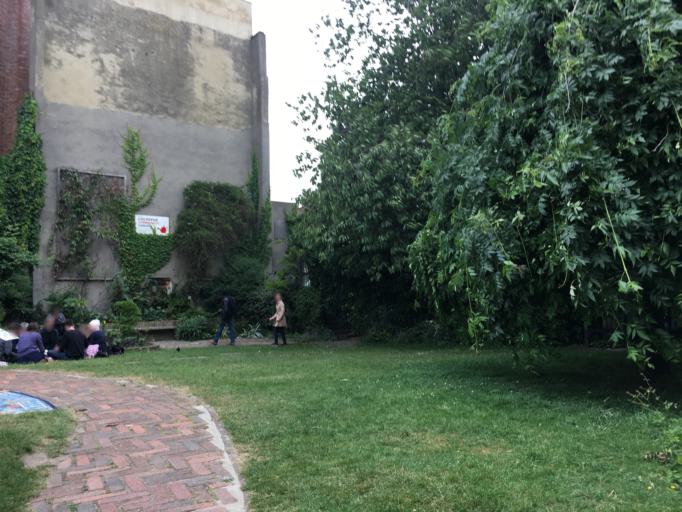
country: GB
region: England
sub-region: Greater London
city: Islington
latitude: 51.5349
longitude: -0.1095
